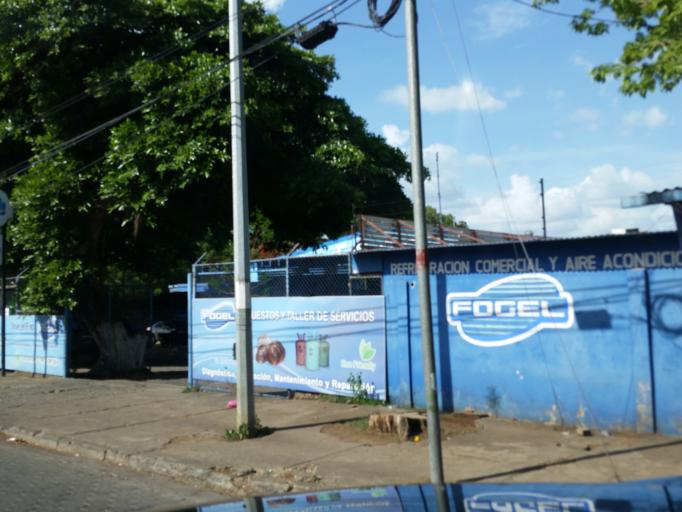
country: NI
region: Managua
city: Managua
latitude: 12.1535
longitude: -86.2239
